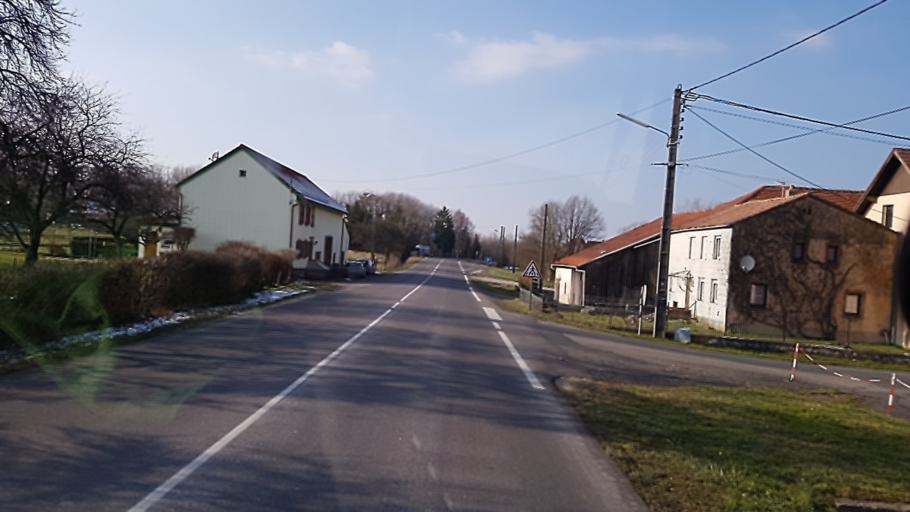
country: FR
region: Alsace
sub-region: Departement du Bas-Rhin
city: Drulingen
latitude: 48.8888
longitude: 7.1356
